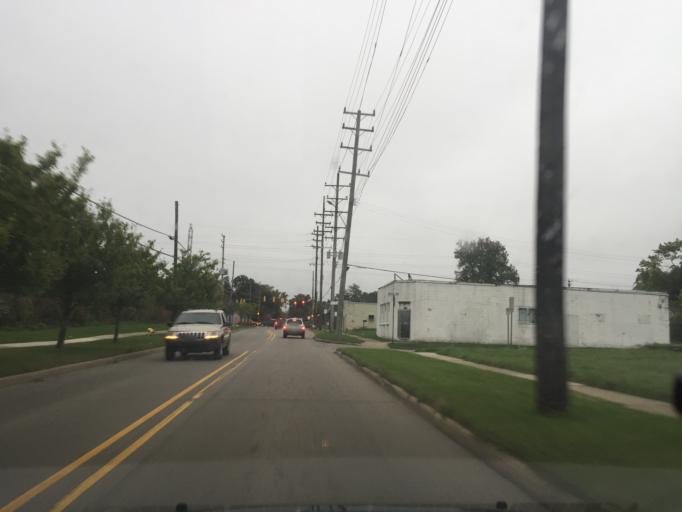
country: US
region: Michigan
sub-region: Oakland County
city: Pontiac
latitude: 42.6206
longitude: -83.2883
